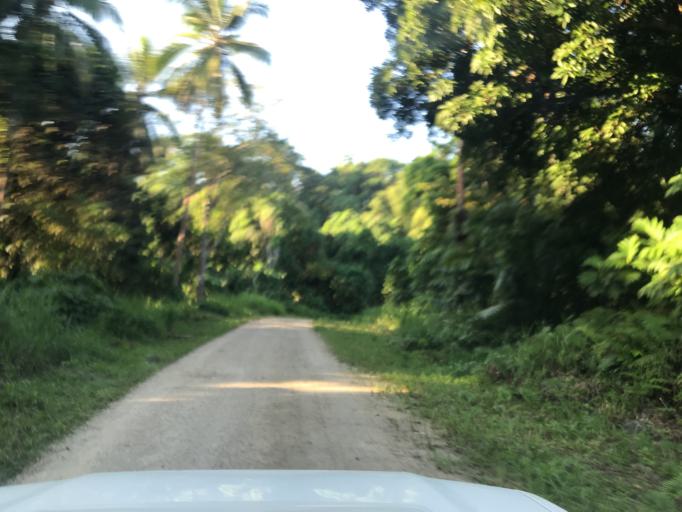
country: VU
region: Sanma
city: Luganville
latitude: -15.5897
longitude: 166.8996
